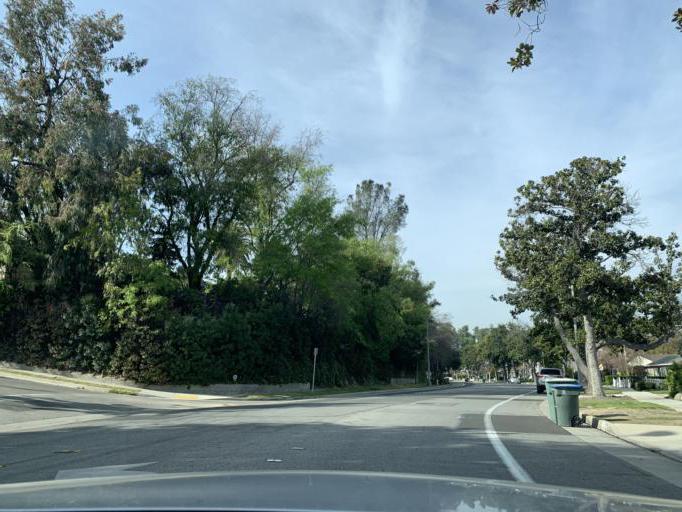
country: US
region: California
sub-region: Los Angeles County
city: South Pasadena
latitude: 34.1370
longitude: -118.1770
